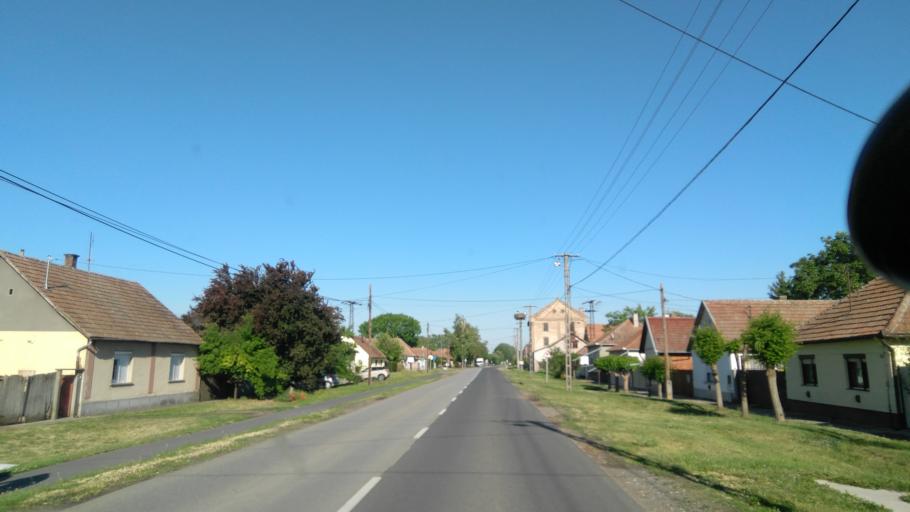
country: HU
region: Bekes
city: Elek
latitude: 46.5320
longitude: 21.2422
